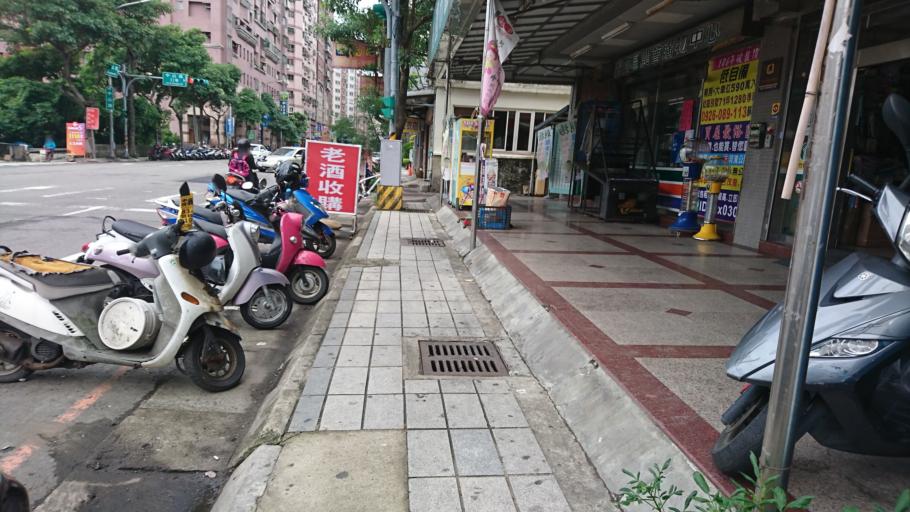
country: TW
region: Taiwan
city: Taoyuan City
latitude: 25.0548
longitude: 121.2991
